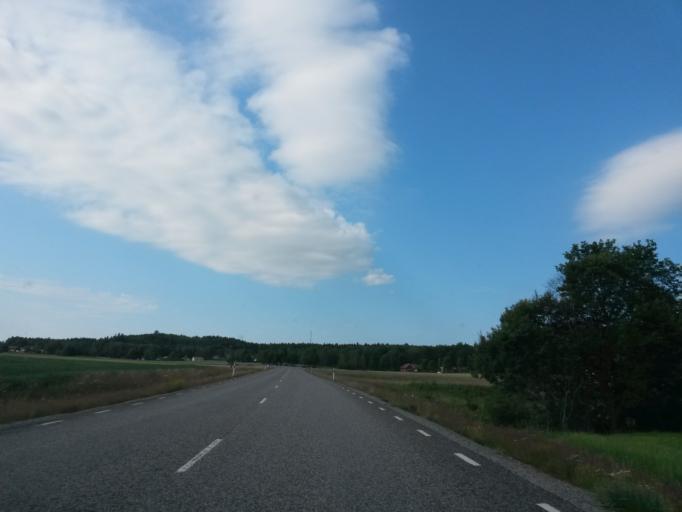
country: SE
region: Vaestra Goetaland
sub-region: Vargarda Kommun
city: Jonstorp
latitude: 58.0350
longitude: 12.6361
